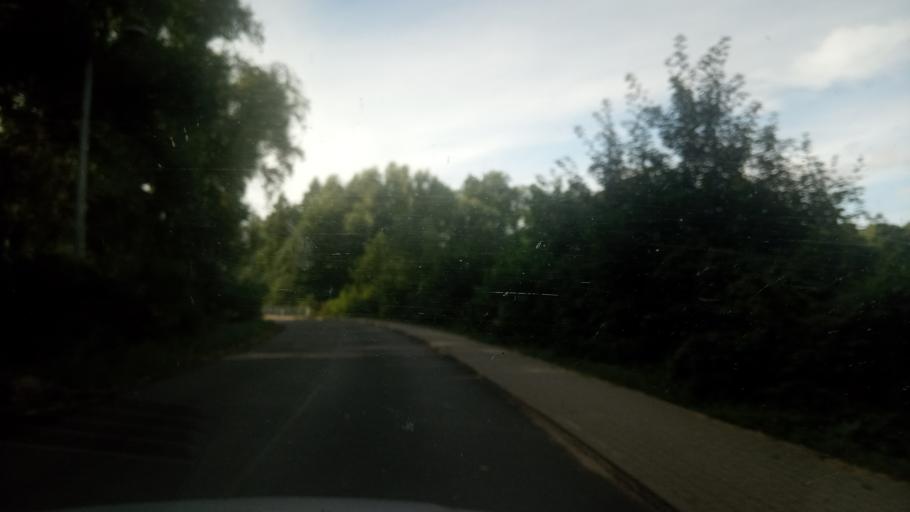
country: PL
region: Kujawsko-Pomorskie
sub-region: Powiat nakielski
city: Sadki
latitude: 53.1937
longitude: 17.3913
